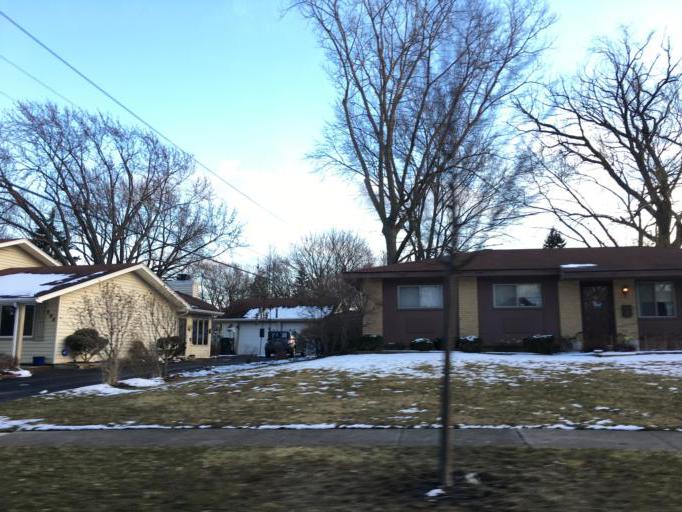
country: US
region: Illinois
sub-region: Cook County
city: Schaumburg
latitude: 42.0424
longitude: -88.0947
